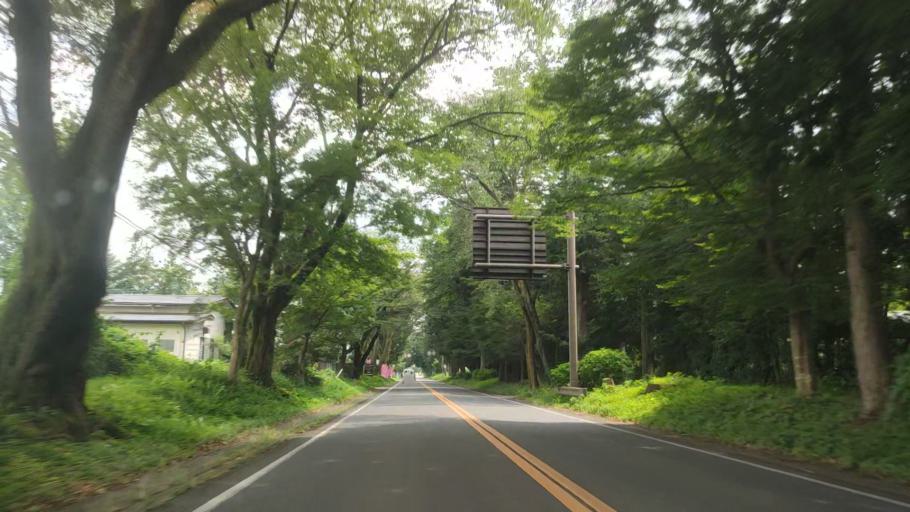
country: JP
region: Tochigi
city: Utsunomiya-shi
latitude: 36.6223
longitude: 139.8531
